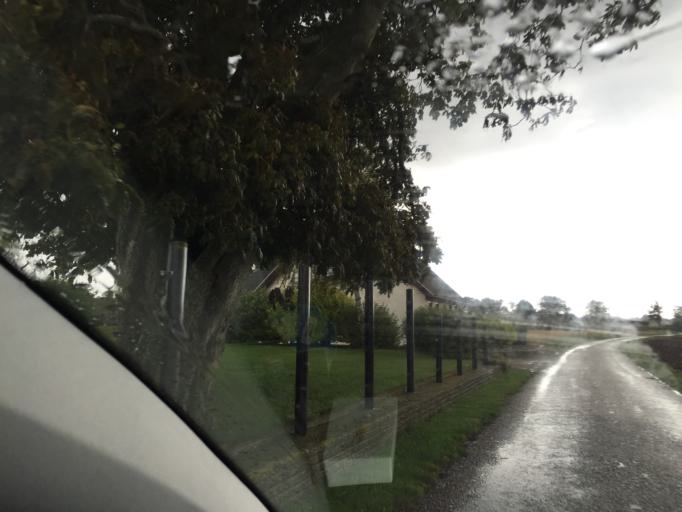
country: DK
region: South Denmark
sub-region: Sonderborg Kommune
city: Dybbol
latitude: 54.9619
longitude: 9.7300
